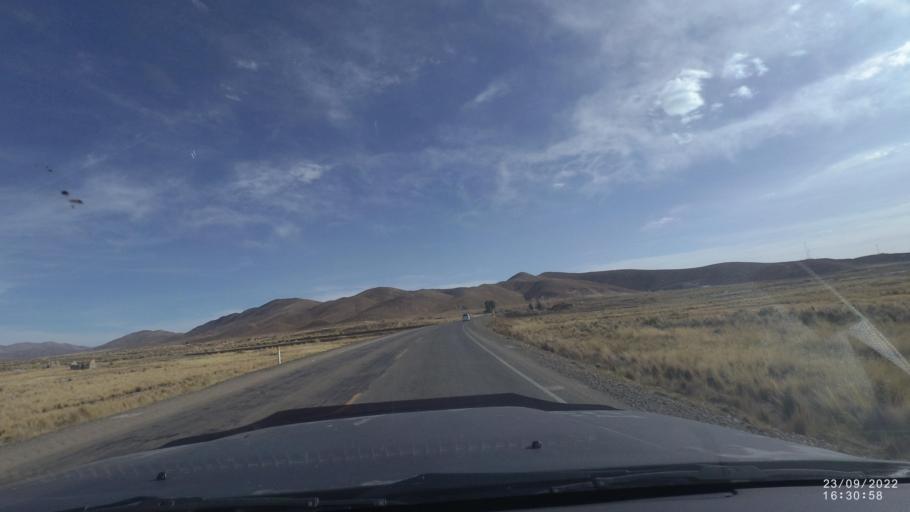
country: BO
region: Oruro
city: Machacamarca
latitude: -18.1614
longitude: -66.9872
